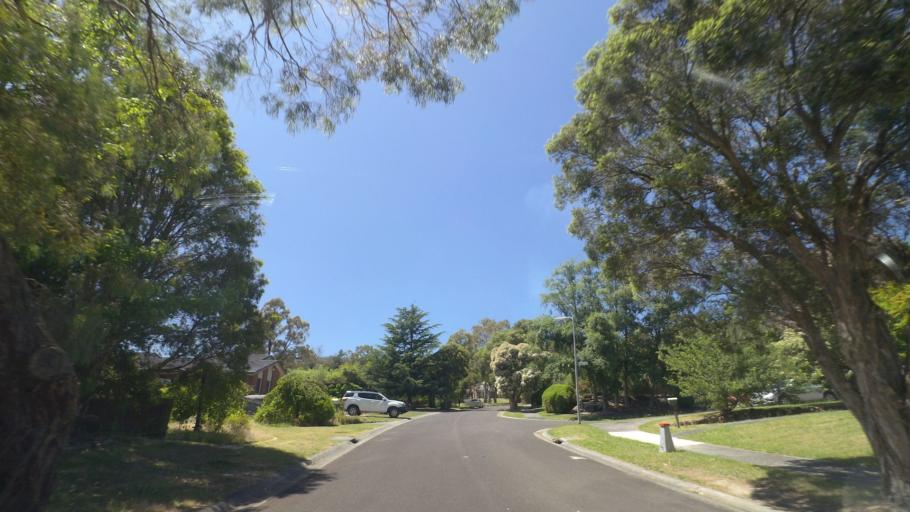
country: AU
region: Victoria
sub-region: Yarra Ranges
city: Montrose
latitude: -37.8099
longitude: 145.3476
